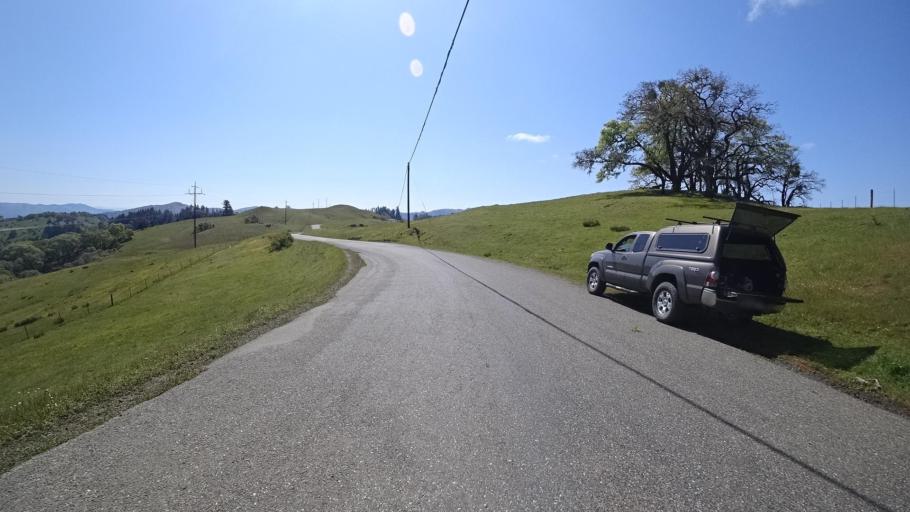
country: US
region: California
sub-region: Humboldt County
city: Redway
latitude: 40.0305
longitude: -123.6370
